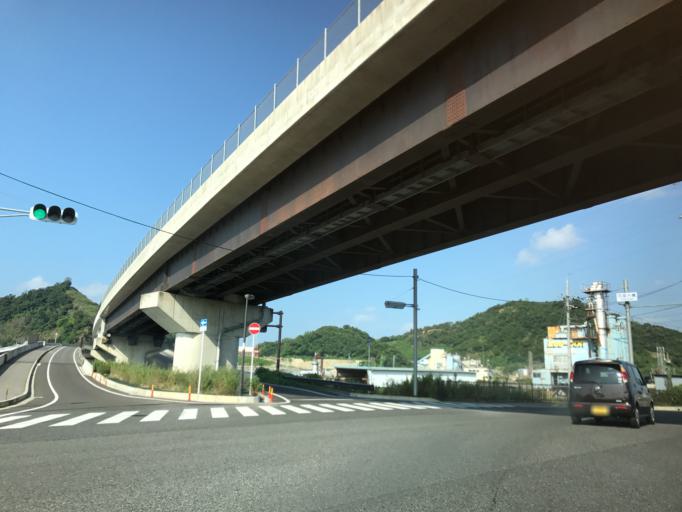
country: JP
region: Shiga Prefecture
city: Moriyama
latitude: 35.0214
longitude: 136.0495
